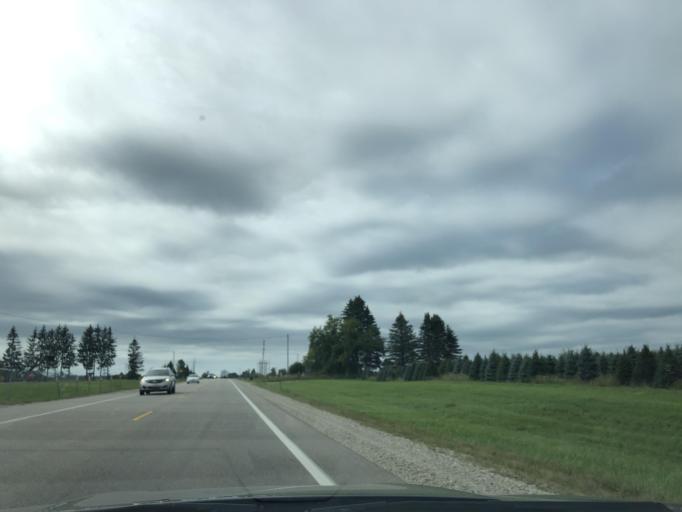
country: US
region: Michigan
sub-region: Missaukee County
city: Lake City
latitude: 44.2757
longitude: -85.2151
